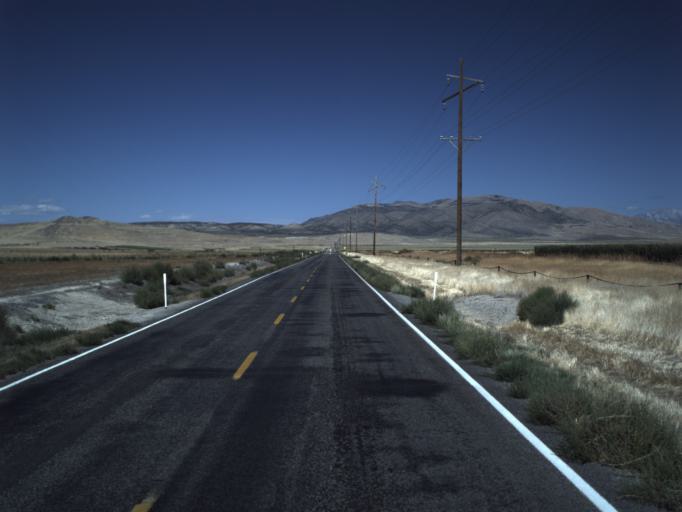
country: US
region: Utah
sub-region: Utah County
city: Genola
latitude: 40.1059
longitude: -111.9591
